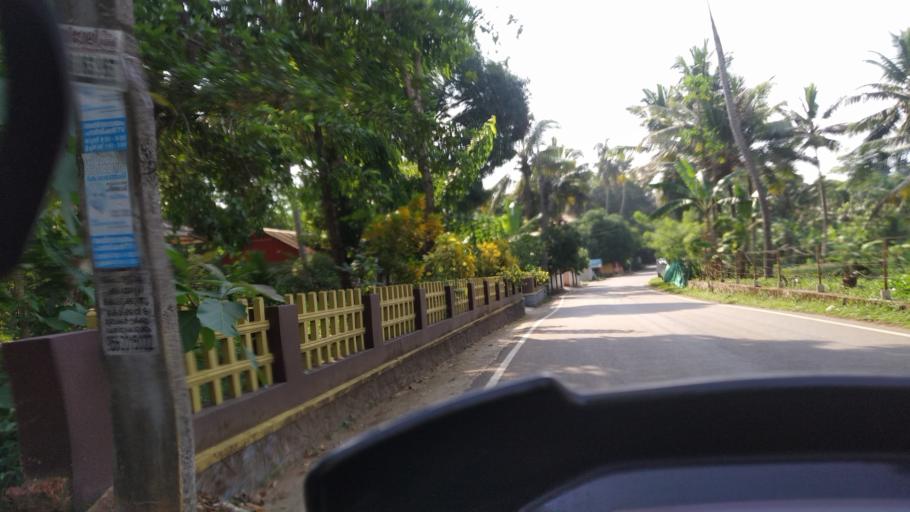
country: IN
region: Kerala
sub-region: Ernakulam
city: Piravam
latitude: 9.8574
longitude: 76.5203
